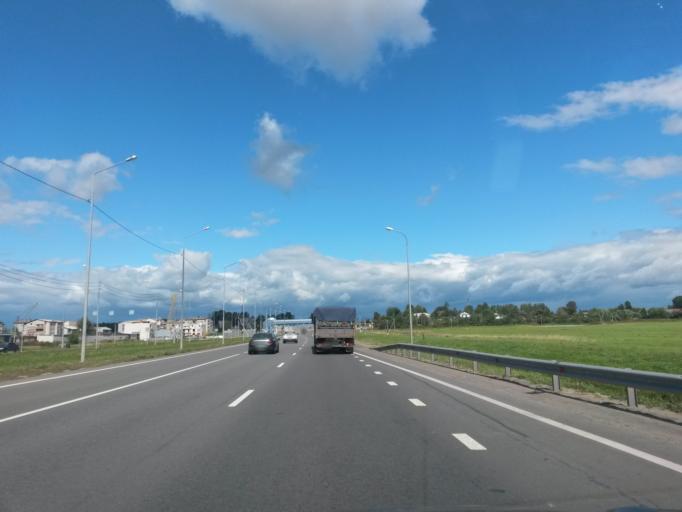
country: RU
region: Jaroslavl
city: Yaroslavl
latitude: 57.6985
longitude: 39.8997
